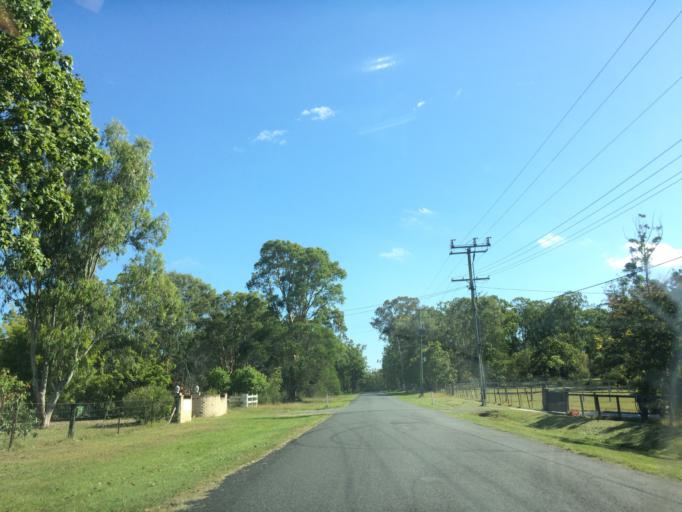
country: AU
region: Queensland
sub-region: Ipswich
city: Springfield Lakes
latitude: -27.7154
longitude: 152.9588
